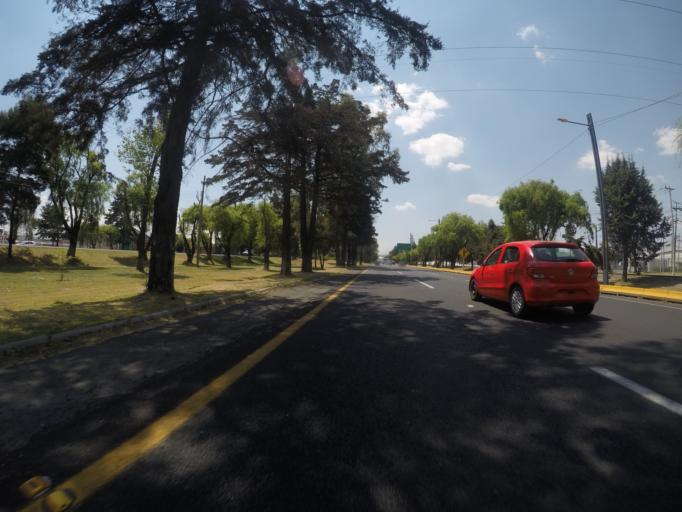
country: MX
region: Mexico
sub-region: San Mateo Atenco
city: Santa Maria la Asuncion
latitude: 19.2866
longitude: -99.5663
